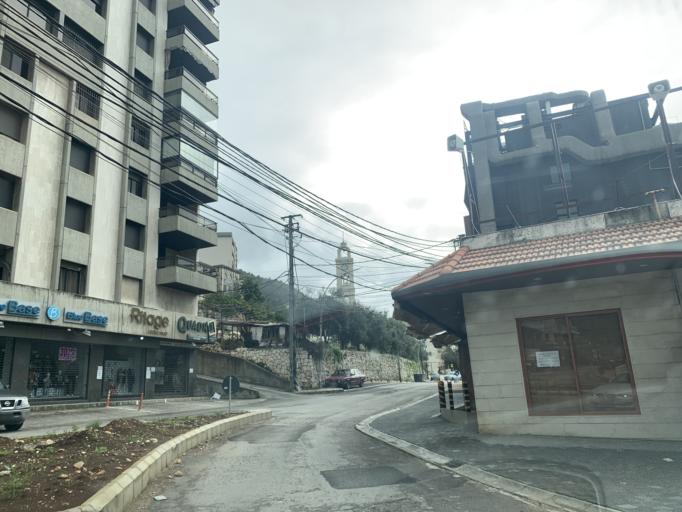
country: LB
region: Mont-Liban
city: Djounie
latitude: 33.9886
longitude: 35.6443
